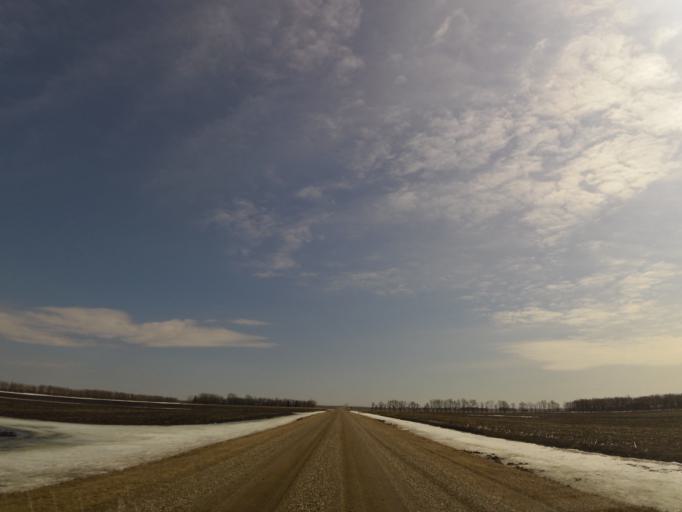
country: US
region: North Dakota
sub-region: Walsh County
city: Grafton
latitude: 48.3243
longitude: -97.2050
